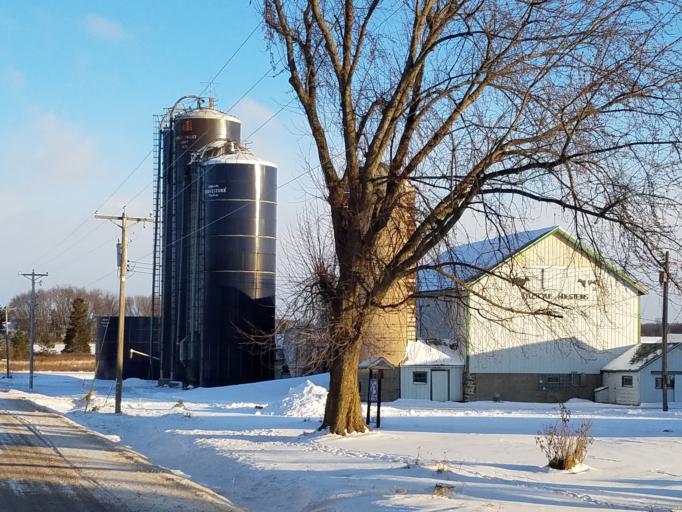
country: US
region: Wisconsin
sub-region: Clark County
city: Loyal
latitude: 44.6094
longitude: -90.4564
